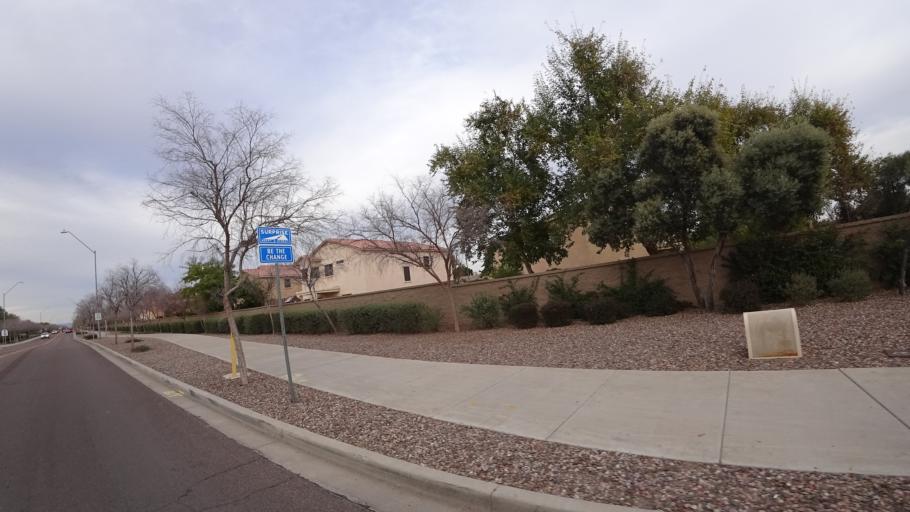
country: US
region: Arizona
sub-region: Maricopa County
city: Citrus Park
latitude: 33.6243
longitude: -112.4268
